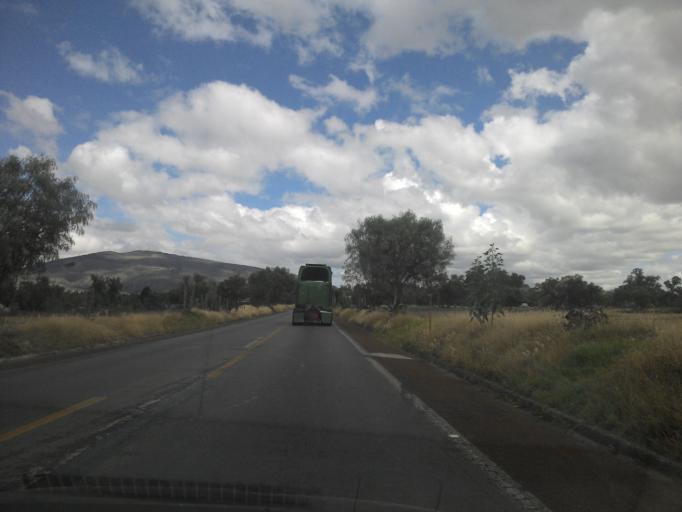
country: MX
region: Morelos
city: Teotihuacan de Arista
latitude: 19.6825
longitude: -98.8573
